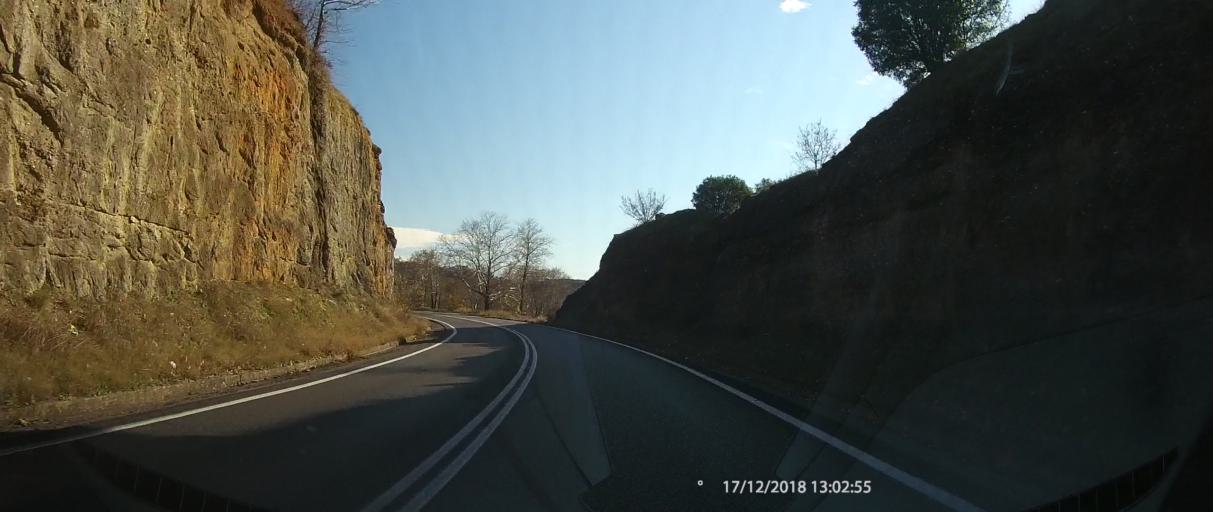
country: GR
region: Thessaly
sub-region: Trikala
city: Kastraki
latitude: 39.7174
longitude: 21.5965
